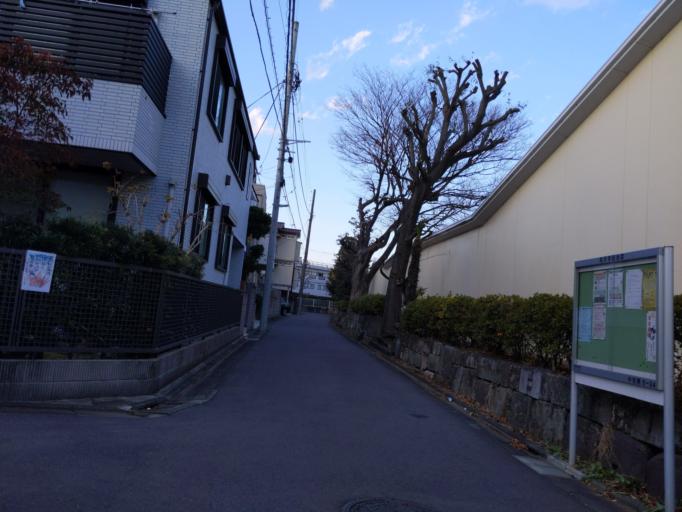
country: JP
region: Tokyo
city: Tokyo
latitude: 35.6358
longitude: 139.6959
